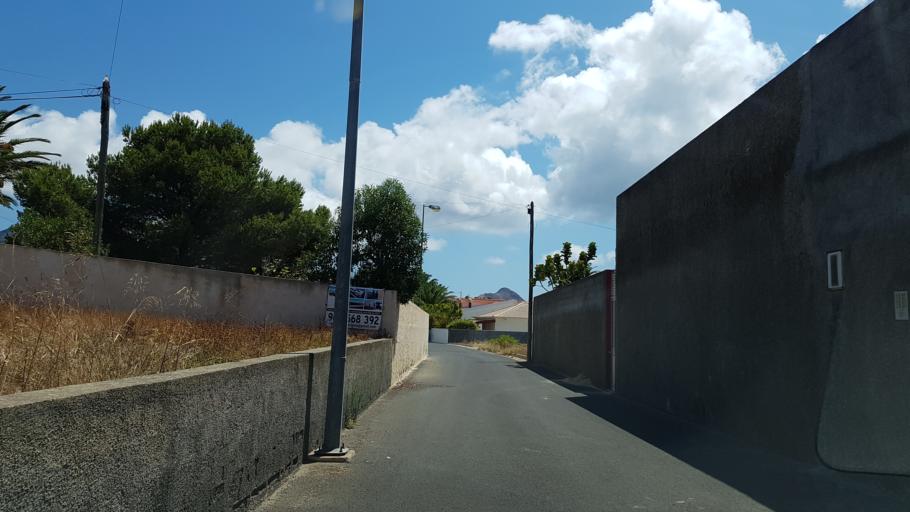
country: PT
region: Madeira
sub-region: Porto Santo
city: Vila de Porto Santo
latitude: 33.0517
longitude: -16.3532
